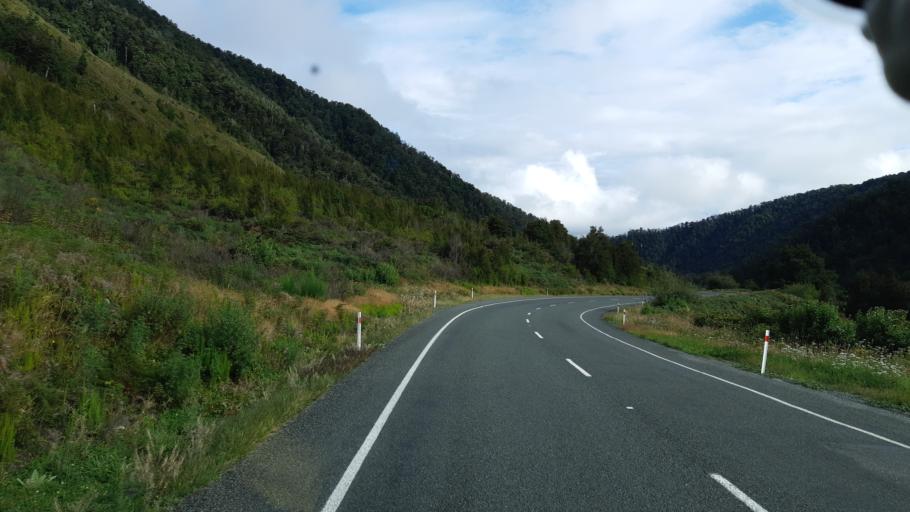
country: NZ
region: West Coast
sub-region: Buller District
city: Westport
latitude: -42.0031
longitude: 172.2293
